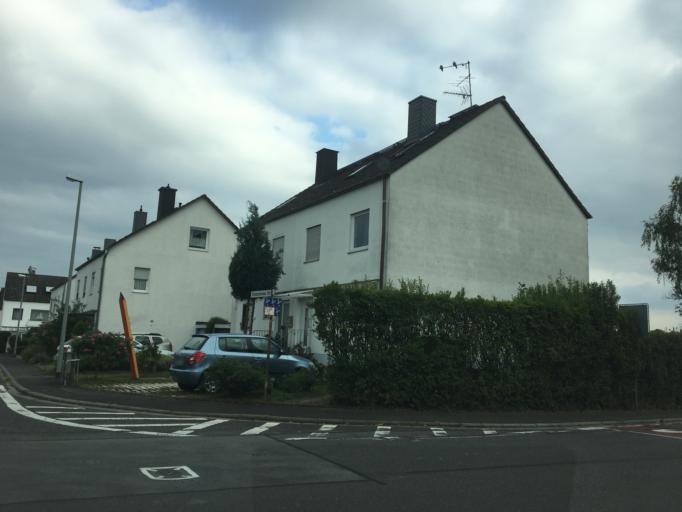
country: DE
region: Hesse
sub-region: Regierungsbezirk Darmstadt
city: Hochheim am Main
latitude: 50.0626
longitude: 8.3651
